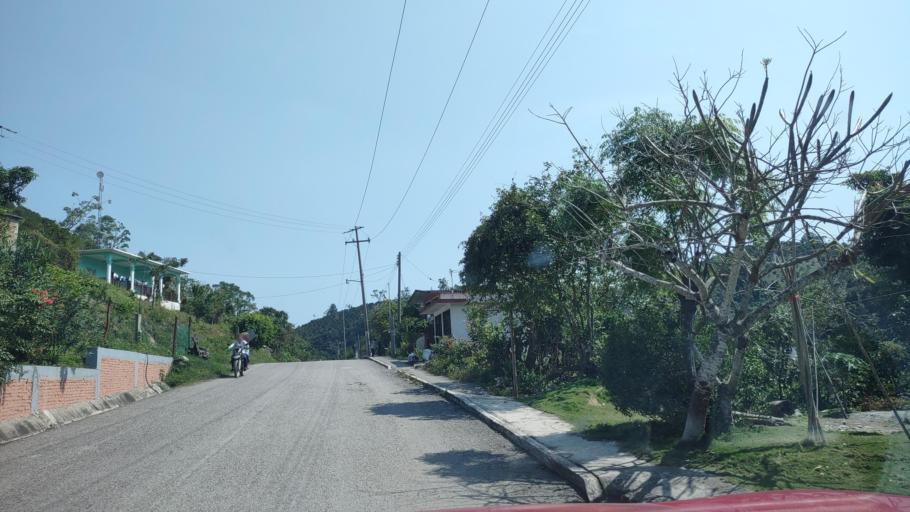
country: MX
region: Veracruz
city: Agua Dulce
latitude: 20.3171
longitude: -97.1748
